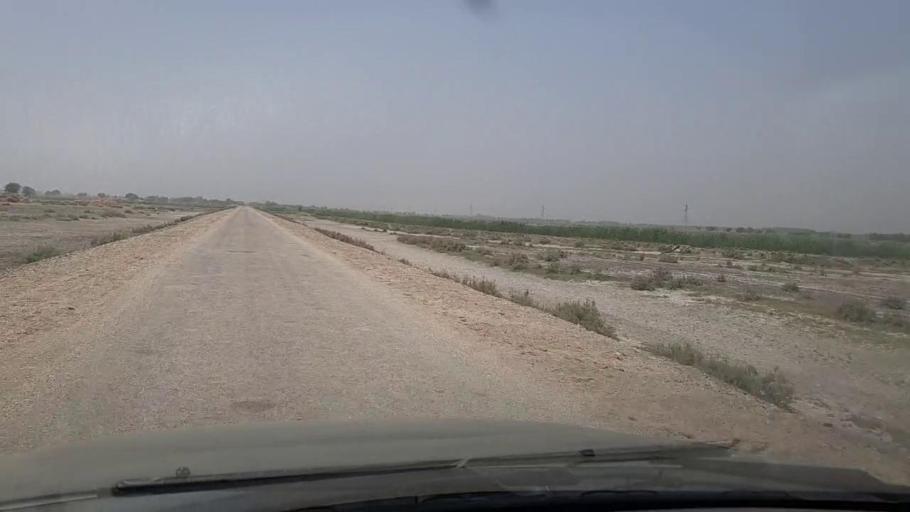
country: PK
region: Sindh
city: Ratodero
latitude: 27.7921
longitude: 68.2310
